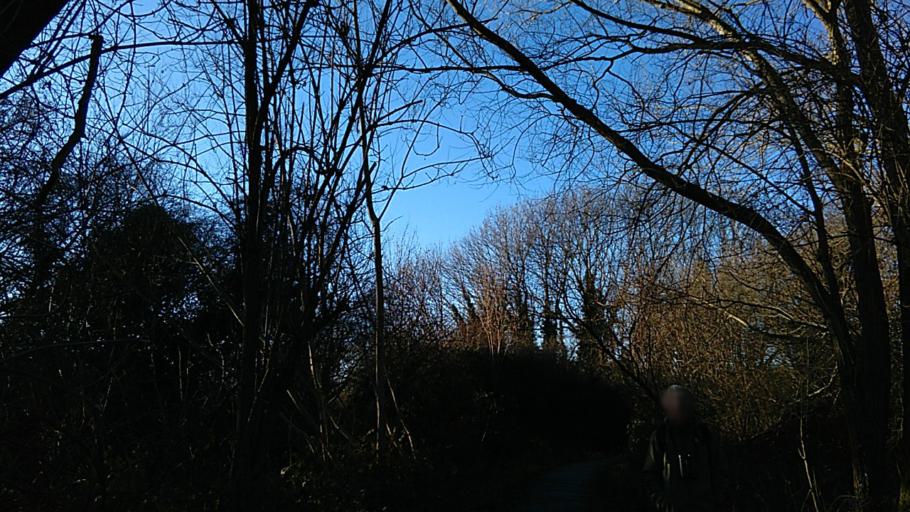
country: GB
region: England
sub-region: Nottinghamshire
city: Gotham
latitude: 52.9130
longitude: -1.2184
